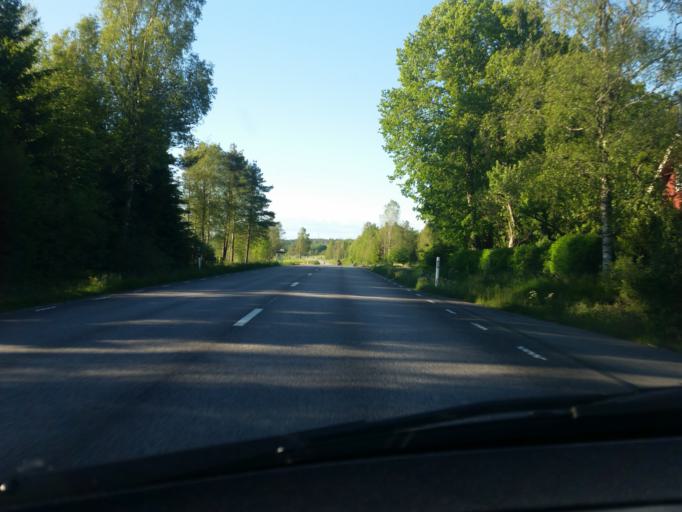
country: SE
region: Vaestra Goetaland
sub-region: Fargelanda Kommun
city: Faergelanda
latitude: 58.5352
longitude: 11.9844
